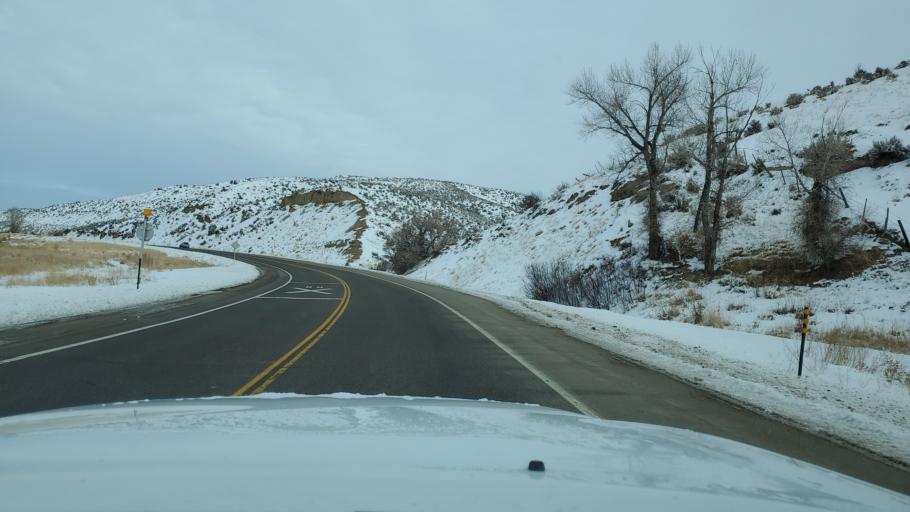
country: US
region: Colorado
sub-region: Routt County
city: Hayden
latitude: 40.5048
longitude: -107.3781
